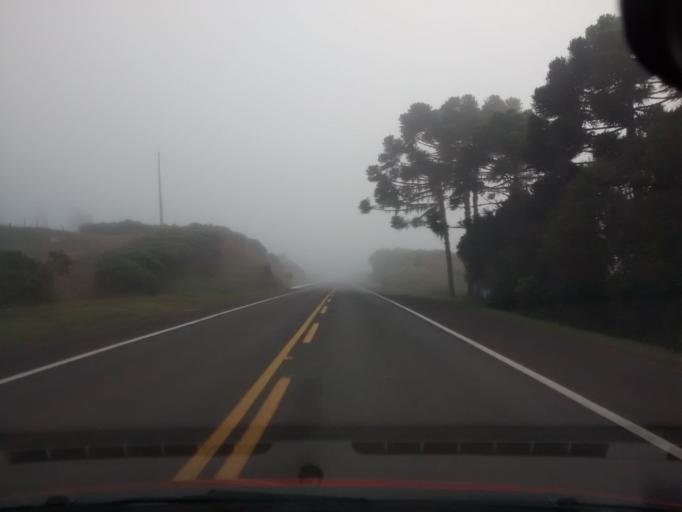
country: BR
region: Rio Grande do Sul
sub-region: Vacaria
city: Vacaria
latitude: -28.3110
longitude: -50.8029
